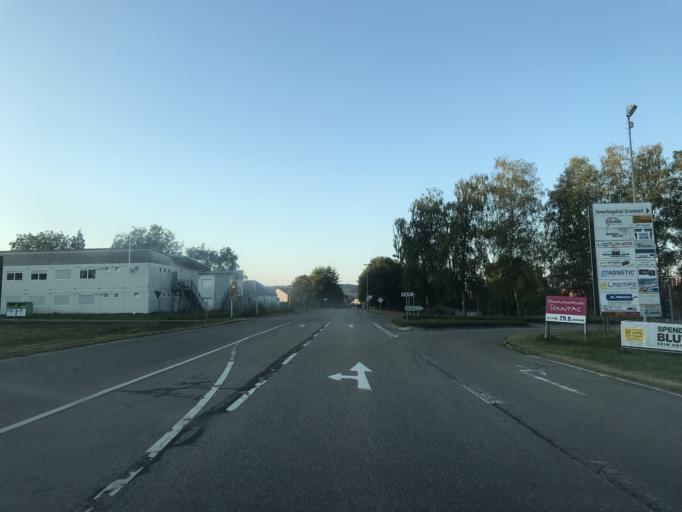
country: DE
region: Baden-Wuerttemberg
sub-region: Freiburg Region
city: Hausen
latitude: 47.6651
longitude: 7.8388
